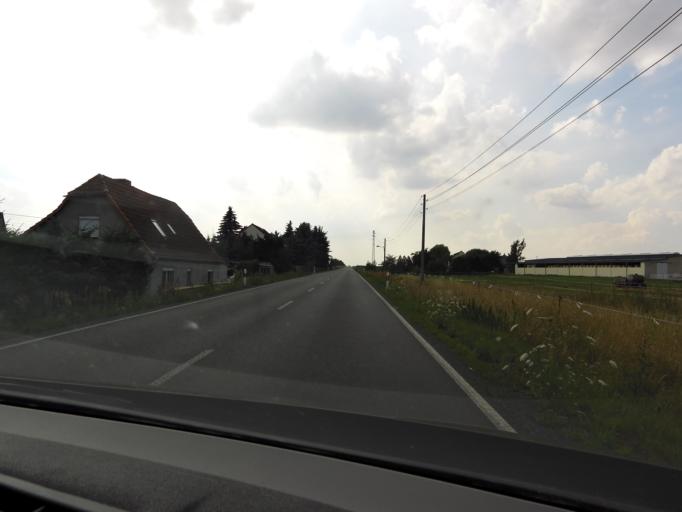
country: DE
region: Saxony
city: Otterwisch
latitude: 51.2393
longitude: 12.6072
